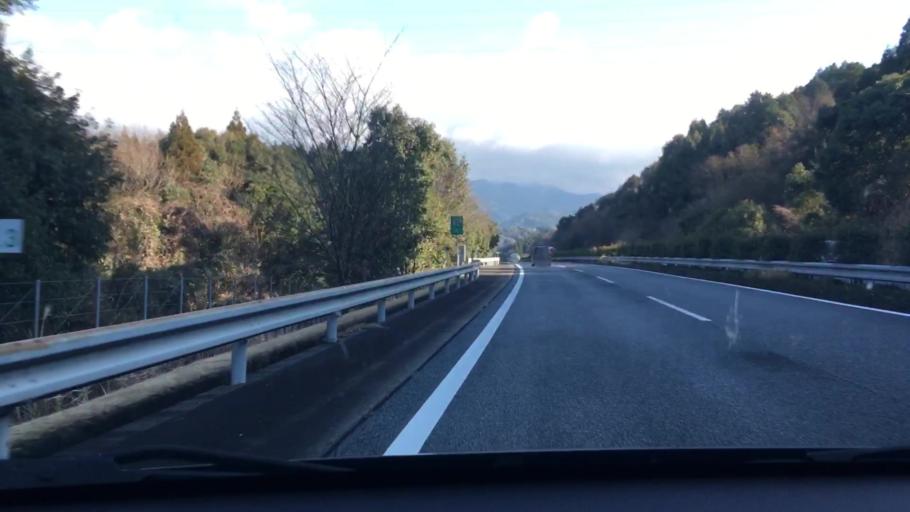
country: JP
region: Kumamoto
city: Hitoyoshi
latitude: 32.1832
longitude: 130.7802
